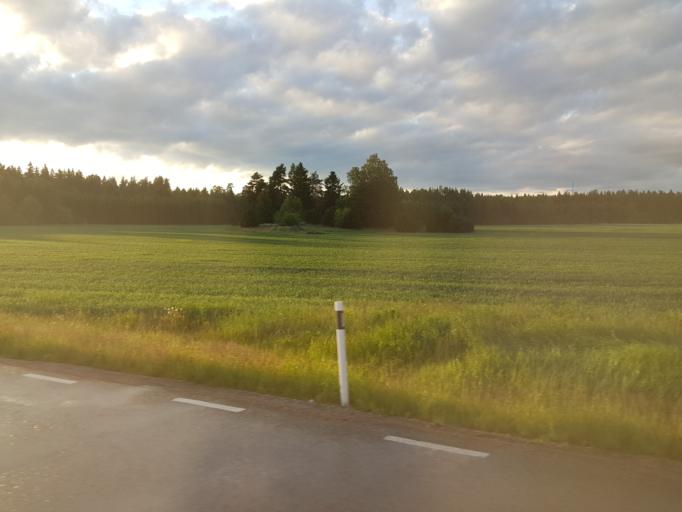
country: SE
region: Uppsala
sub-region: Uppsala Kommun
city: Vattholma
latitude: 59.9522
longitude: 17.8701
